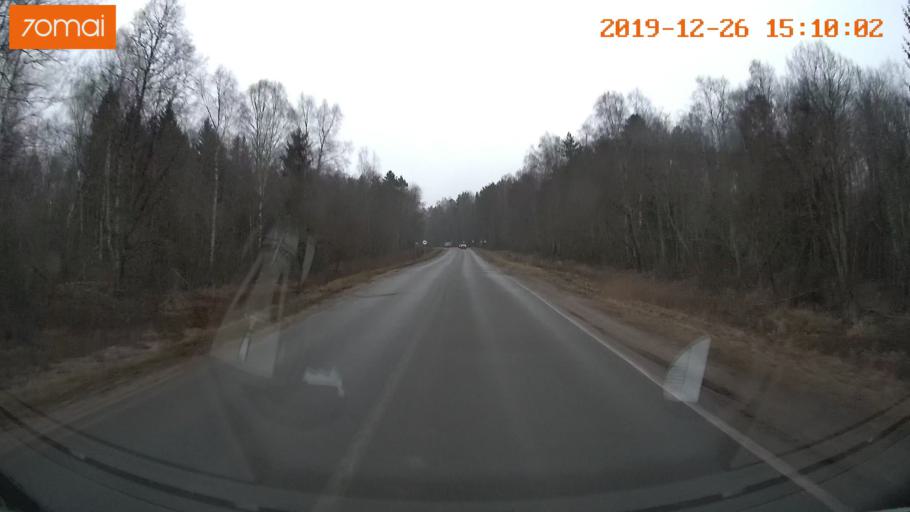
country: RU
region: Jaroslavl
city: Rybinsk
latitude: 58.1438
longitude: 38.8468
